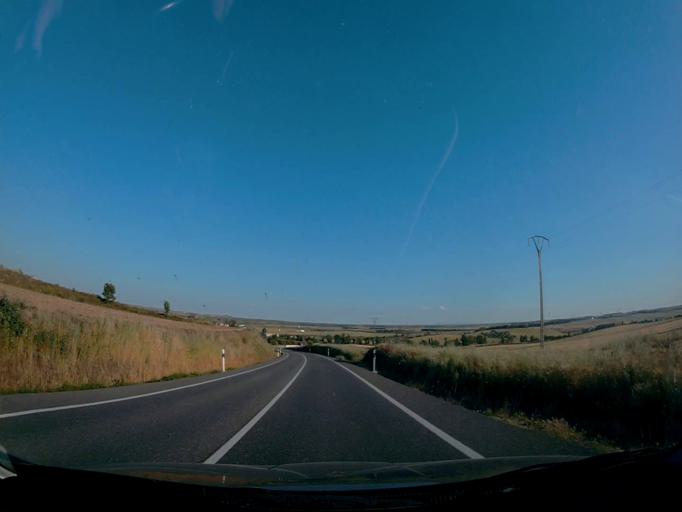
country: ES
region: Castille-La Mancha
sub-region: Province of Toledo
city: Maqueda
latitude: 40.0676
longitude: -4.3778
